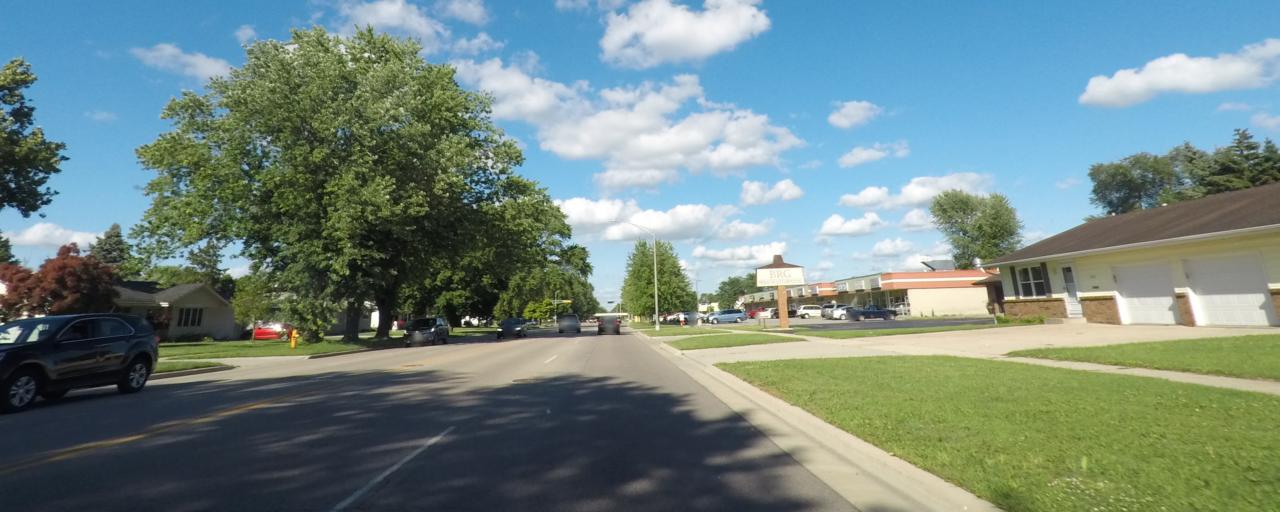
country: US
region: Wisconsin
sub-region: Rock County
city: Janesville
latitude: 42.6949
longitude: -88.9900
